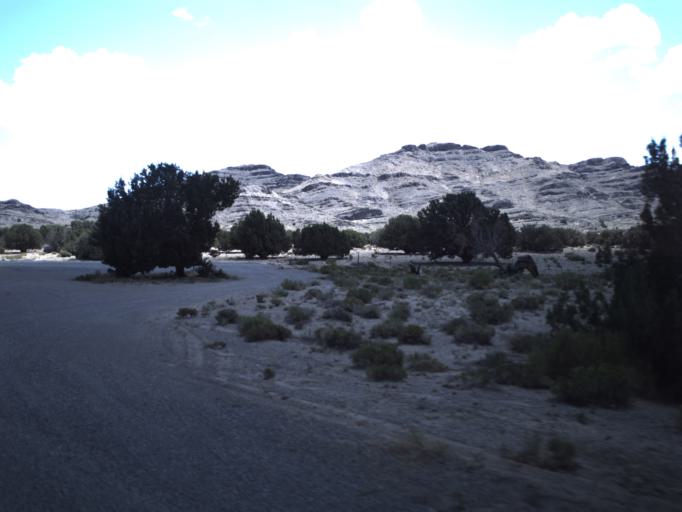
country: US
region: Utah
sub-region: Beaver County
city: Milford
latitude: 39.0733
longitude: -113.7197
